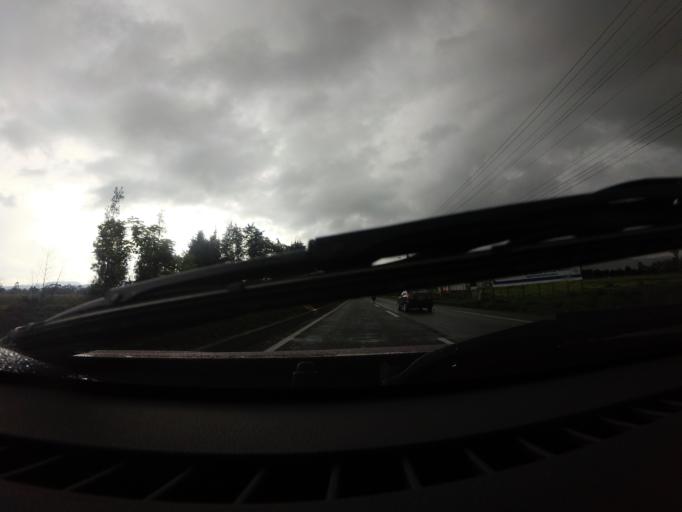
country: CO
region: Cundinamarca
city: El Rosal
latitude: 4.8416
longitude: -74.2607
